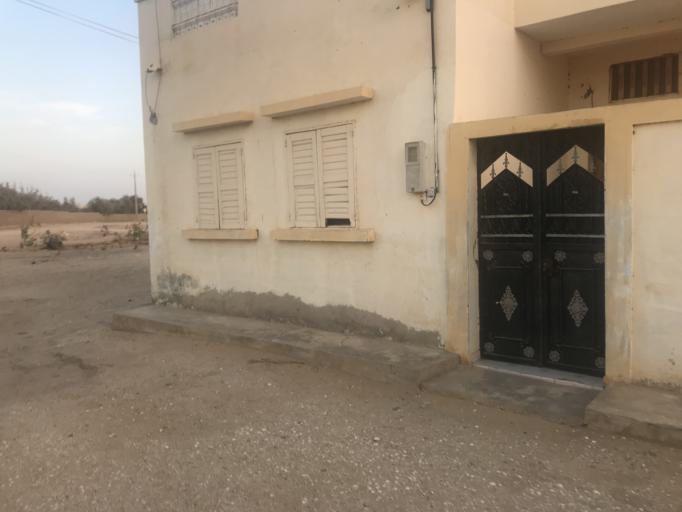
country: SN
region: Saint-Louis
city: Saint-Louis
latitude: 16.0512
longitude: -16.4342
